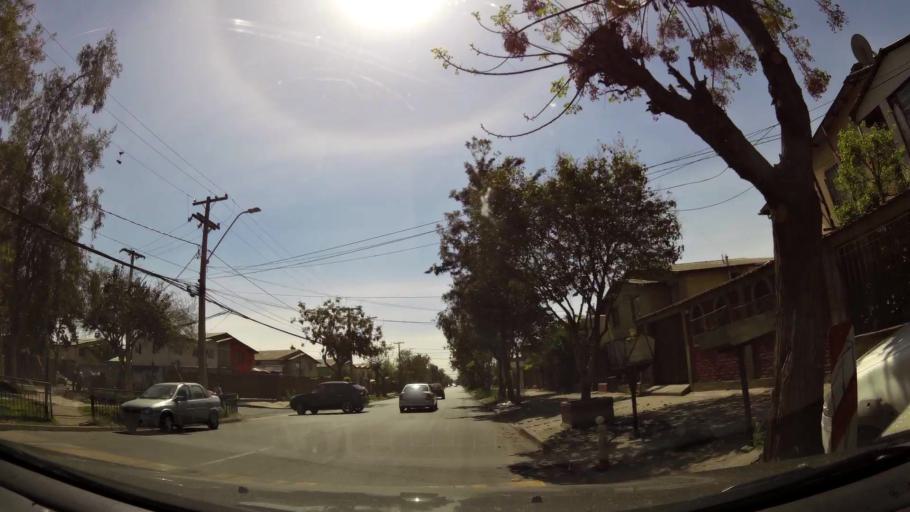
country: CL
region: Santiago Metropolitan
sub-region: Provincia de Cordillera
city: Puente Alto
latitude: -33.5709
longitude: -70.5615
